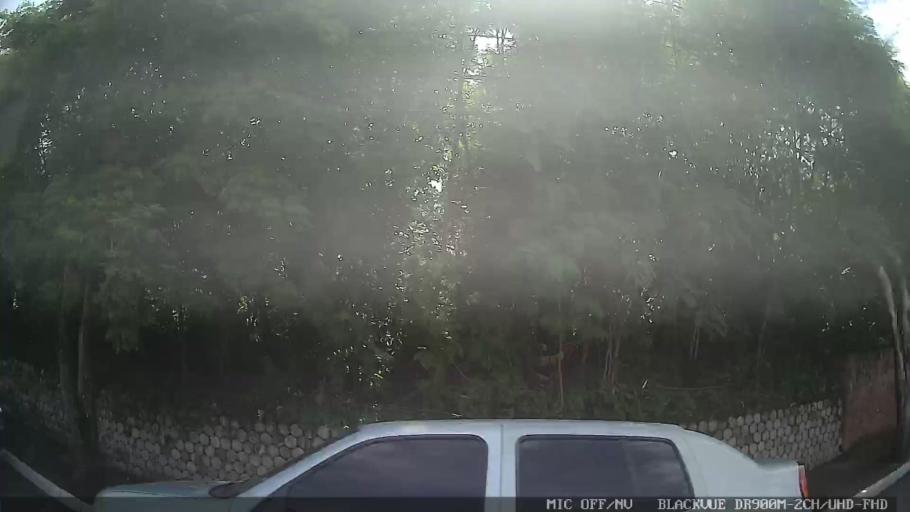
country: BR
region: Sao Paulo
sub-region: Laranjal Paulista
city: Laranjal Paulista
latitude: -23.0363
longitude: -47.8354
